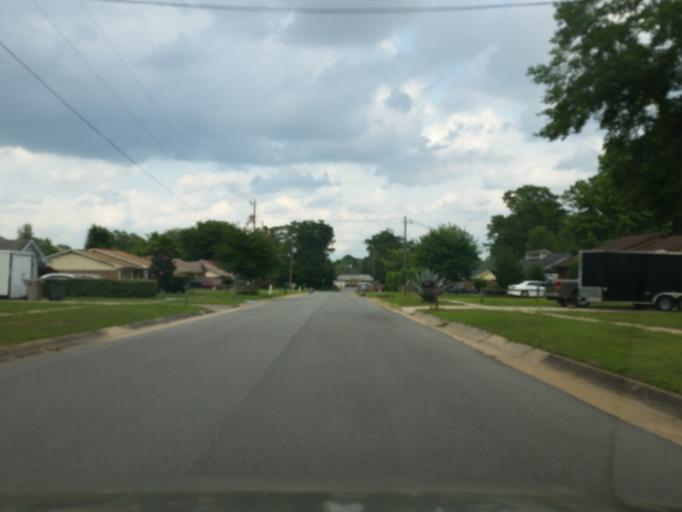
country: US
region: Florida
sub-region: Escambia County
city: Ferry Pass
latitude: 30.5174
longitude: -87.1866
